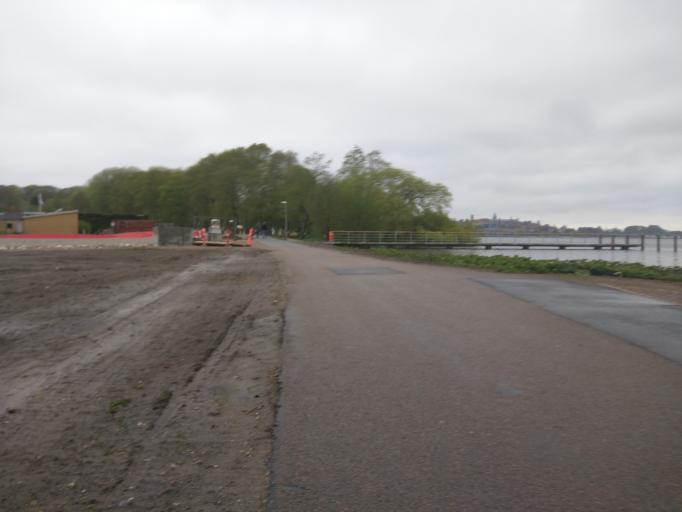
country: DK
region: Central Jutland
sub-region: Viborg Kommune
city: Viborg
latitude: 56.4369
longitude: 9.4058
